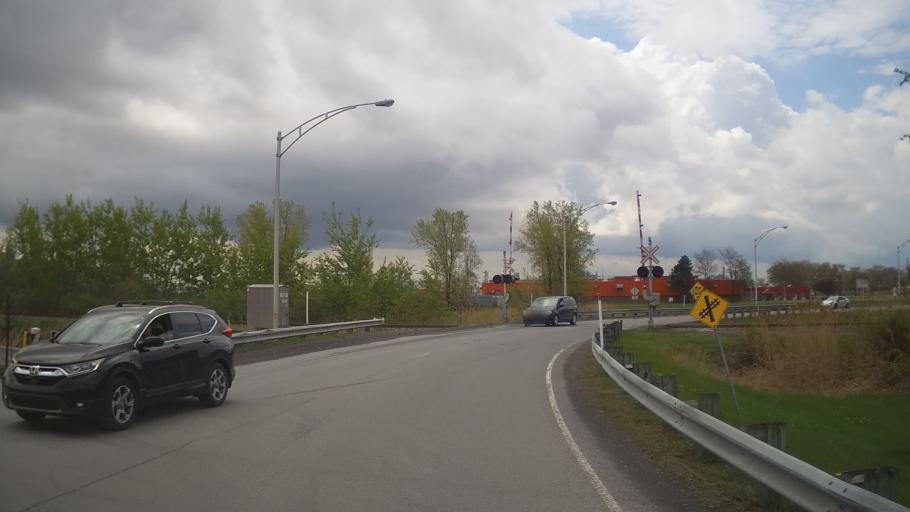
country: CA
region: Quebec
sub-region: Monteregie
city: Saint-Jean-sur-Richelieu
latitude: 45.3121
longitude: -73.2198
